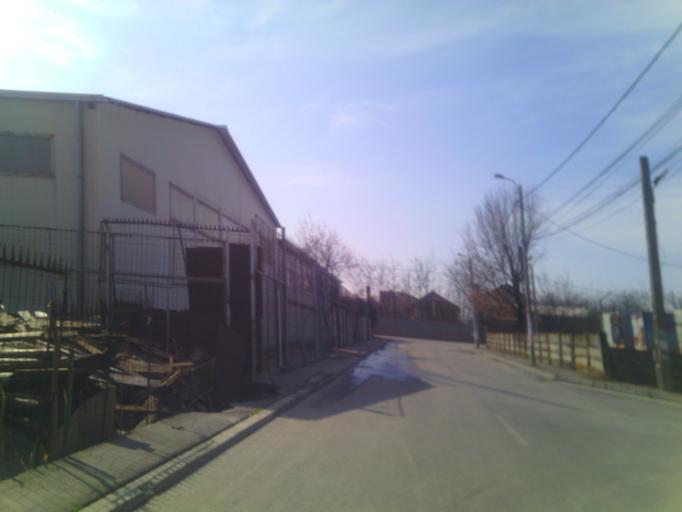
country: RO
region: Ilfov
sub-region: Comuna Jilava
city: Jilava
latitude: 44.3680
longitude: 26.1016
